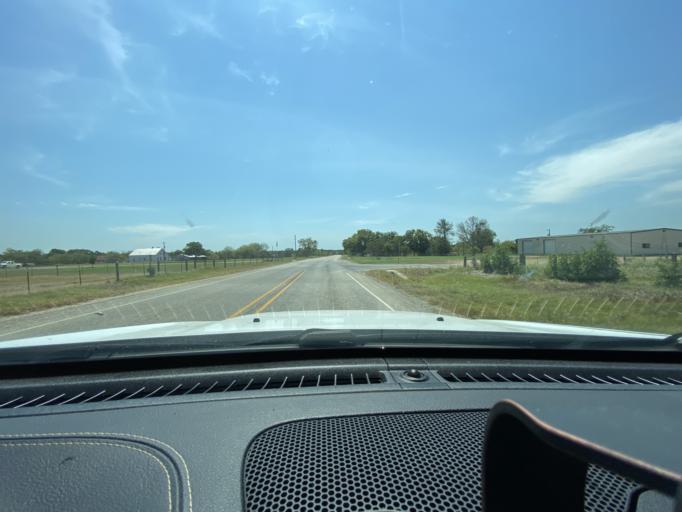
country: US
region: Texas
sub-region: Lee County
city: Giddings
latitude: 30.1281
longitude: -96.9993
